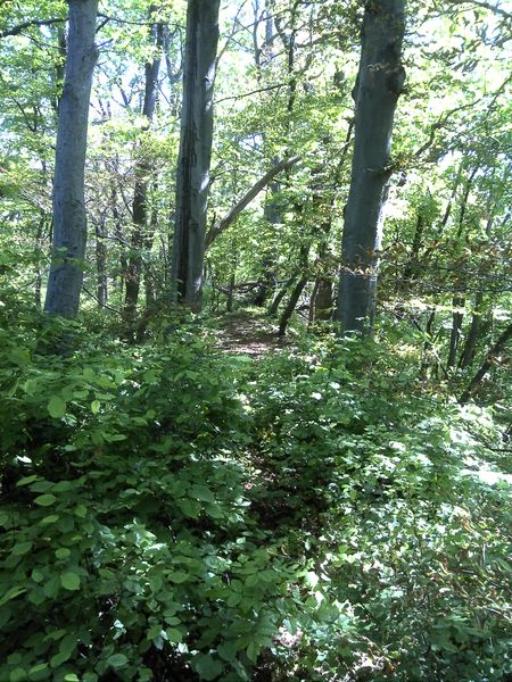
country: HU
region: Baranya
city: Pellerd
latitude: 46.0891
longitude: 18.1482
